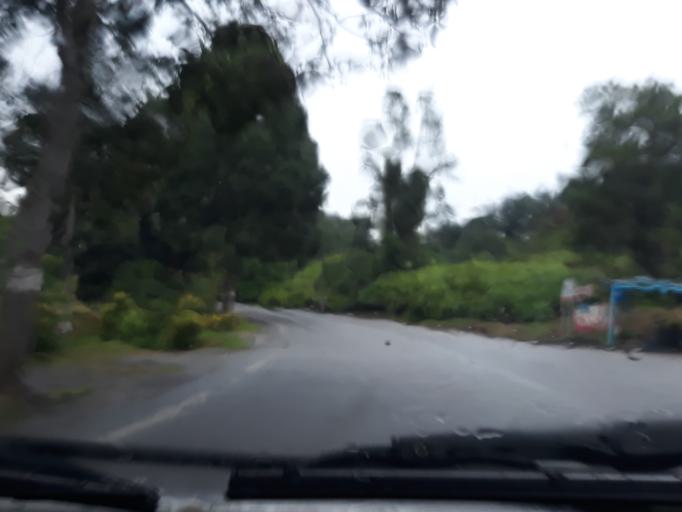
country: MY
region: Penang
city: Nibong Tebal
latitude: 5.2184
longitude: 100.6095
